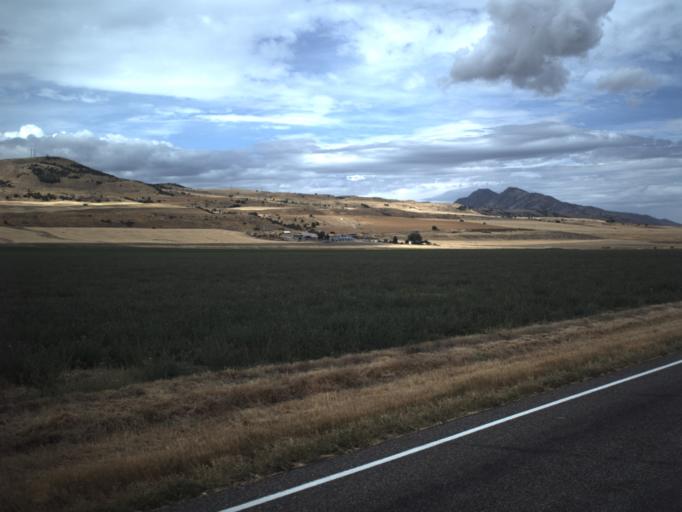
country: US
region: Utah
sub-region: Cache County
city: Benson
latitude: 41.8165
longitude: -111.9970
